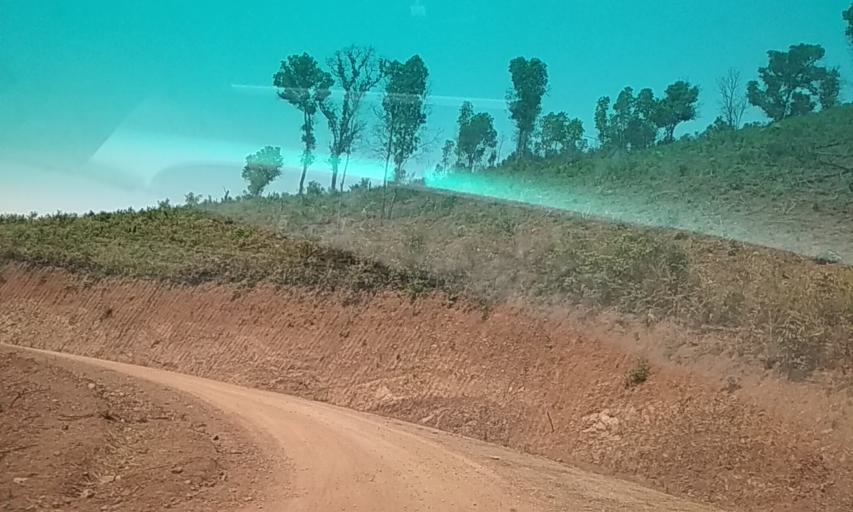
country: VN
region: Huyen Dien Bien
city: Dien Bien Phu
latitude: 21.4833
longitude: 102.7790
